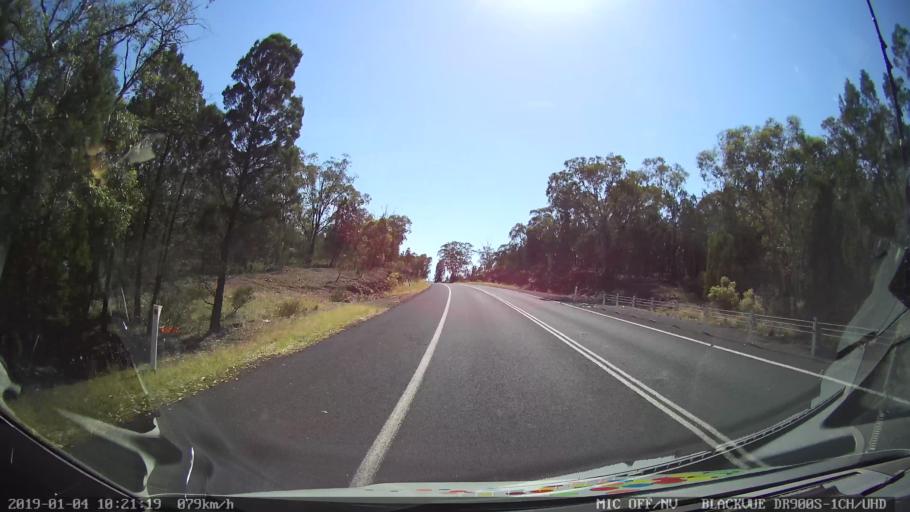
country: AU
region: New South Wales
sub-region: Cabonne
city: Canowindra
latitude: -33.3734
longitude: 148.5088
